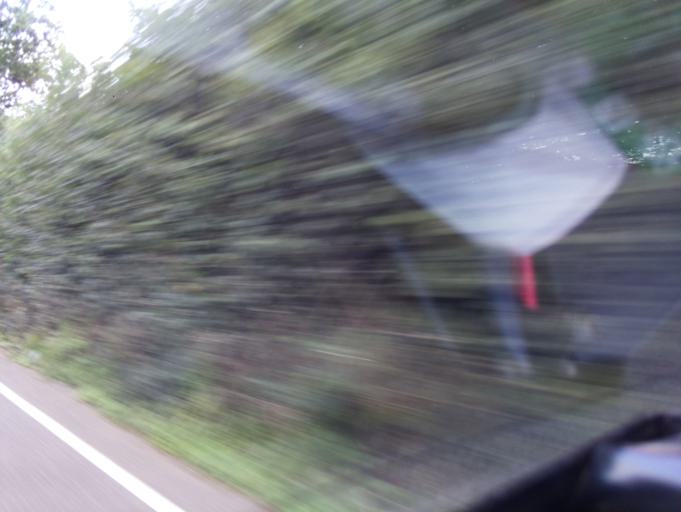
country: GB
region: England
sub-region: Devon
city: Sidmouth
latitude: 50.7270
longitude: -3.2159
